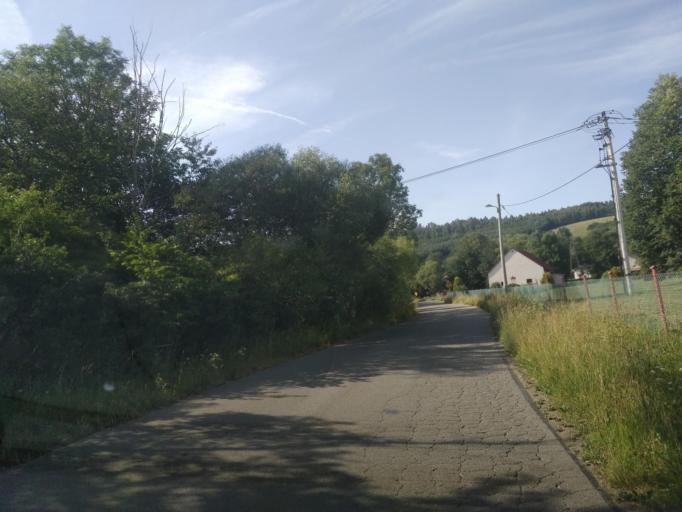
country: PL
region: Subcarpathian Voivodeship
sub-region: Powiat krosnienski
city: Jasliska
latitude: 49.4271
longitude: 21.8520
